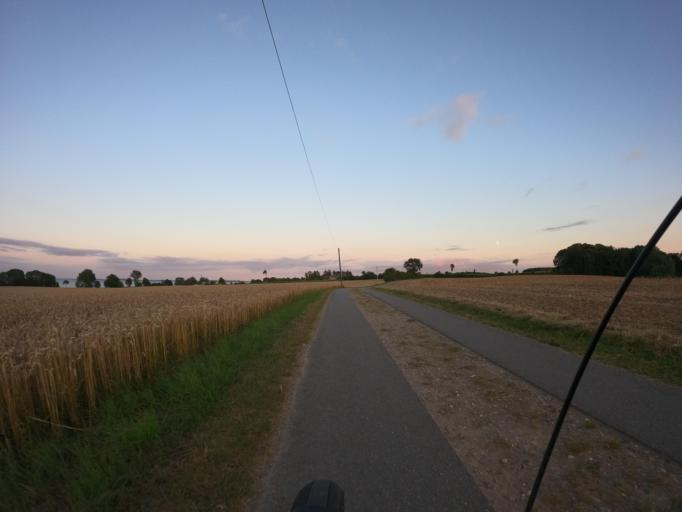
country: DE
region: Schleswig-Holstein
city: Steinberg
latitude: 54.7882
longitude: 9.7916
